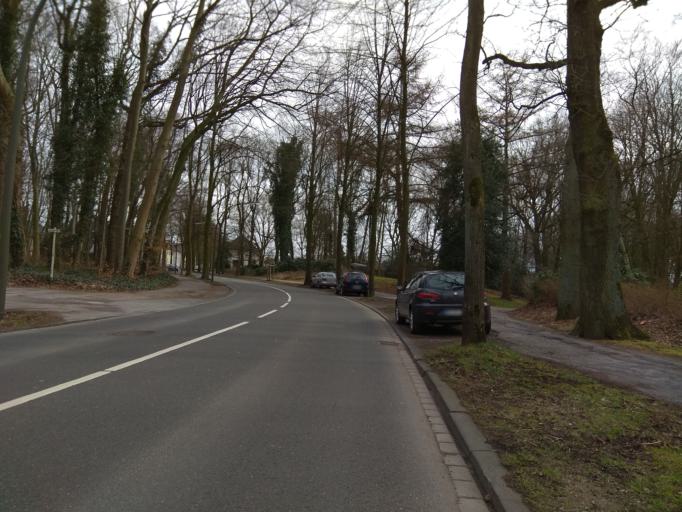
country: DE
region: North Rhine-Westphalia
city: Marl
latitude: 51.6600
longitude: 7.1345
